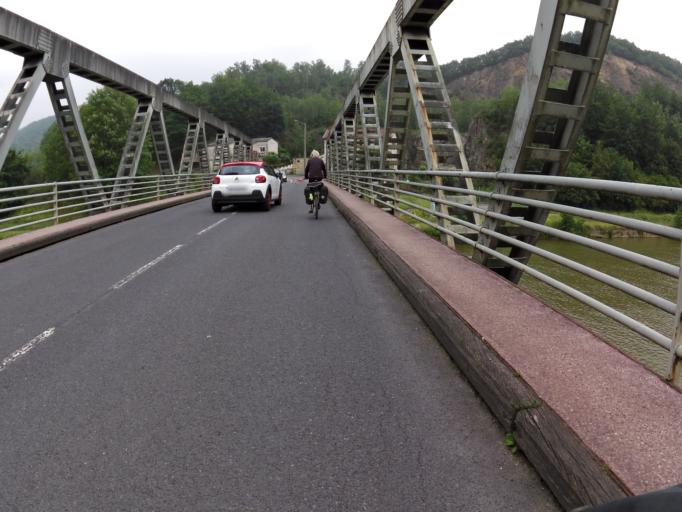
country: FR
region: Champagne-Ardenne
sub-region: Departement des Ardennes
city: Fumay
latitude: 49.9942
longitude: 4.7039
